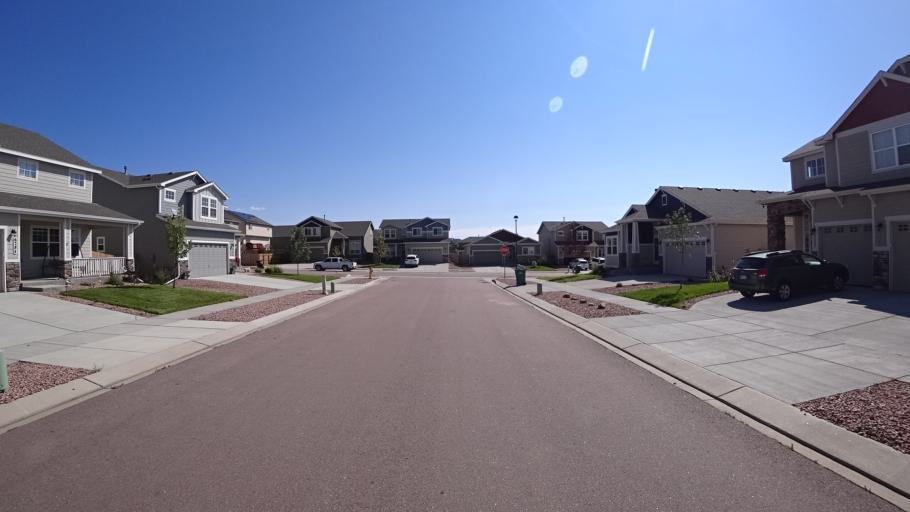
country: US
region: Colorado
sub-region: El Paso County
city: Cimarron Hills
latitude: 38.9322
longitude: -104.7103
